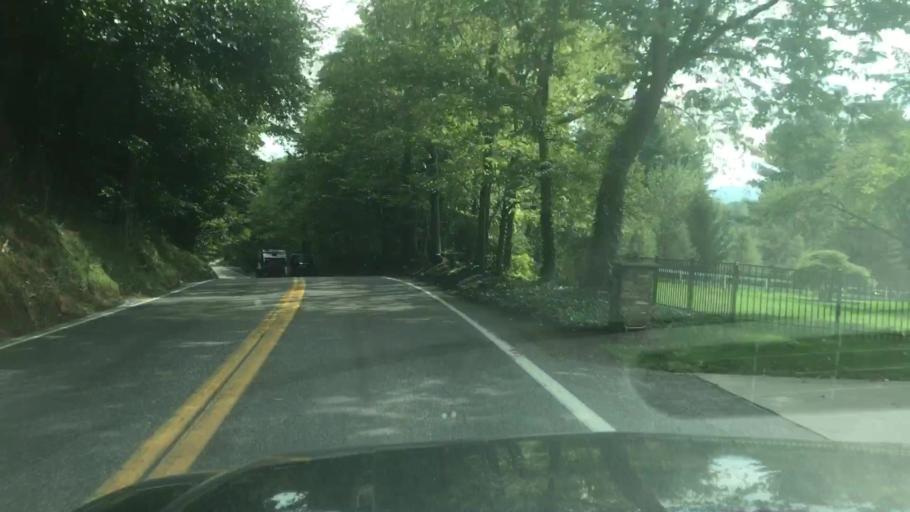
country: US
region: Pennsylvania
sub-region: Cumberland County
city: Shiremanstown
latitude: 40.1872
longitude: -76.9355
